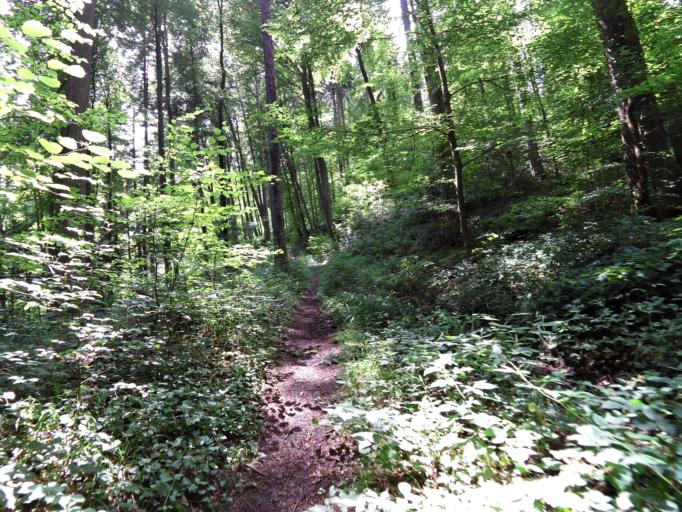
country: CH
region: Thurgau
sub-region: Kreuzlingen District
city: Ermatingen
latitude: 47.6605
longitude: 9.0760
